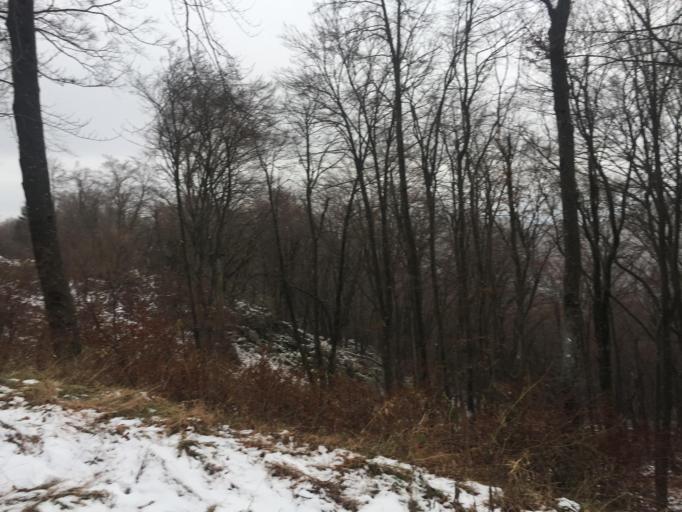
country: SI
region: Kanal
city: Kanal
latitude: 46.0601
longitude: 13.6736
